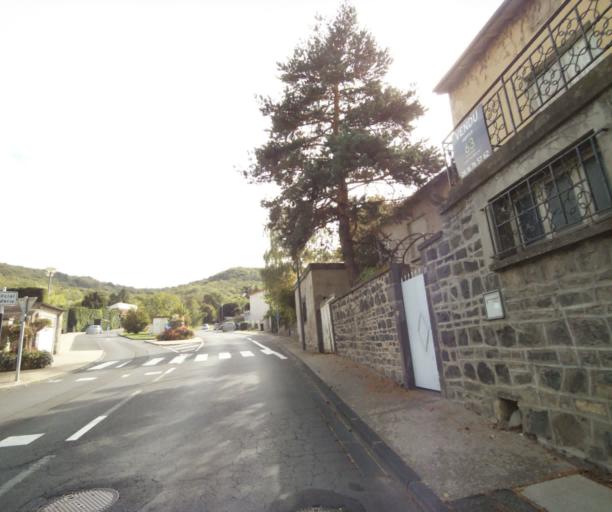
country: FR
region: Auvergne
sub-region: Departement du Puy-de-Dome
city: Romagnat
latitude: 45.7272
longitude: 3.1008
